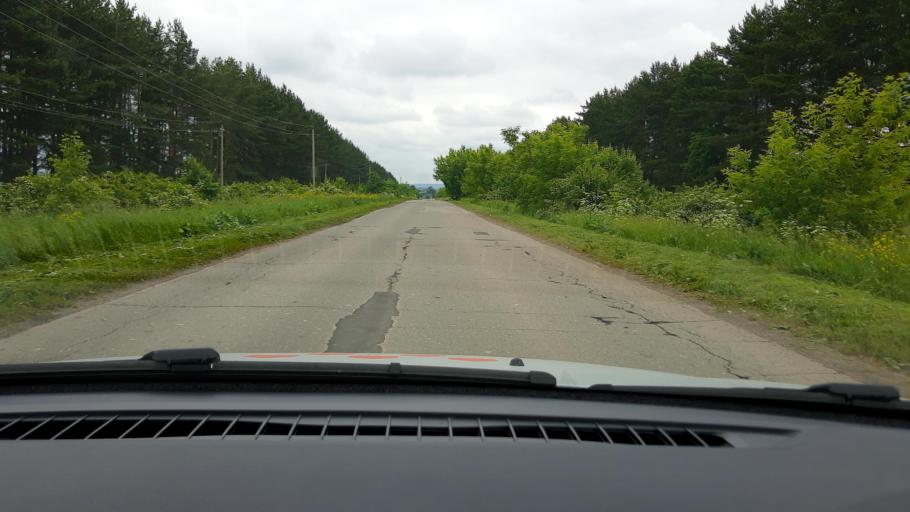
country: RU
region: Nizjnij Novgorod
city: Bogorodsk
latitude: 56.0820
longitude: 43.5118
